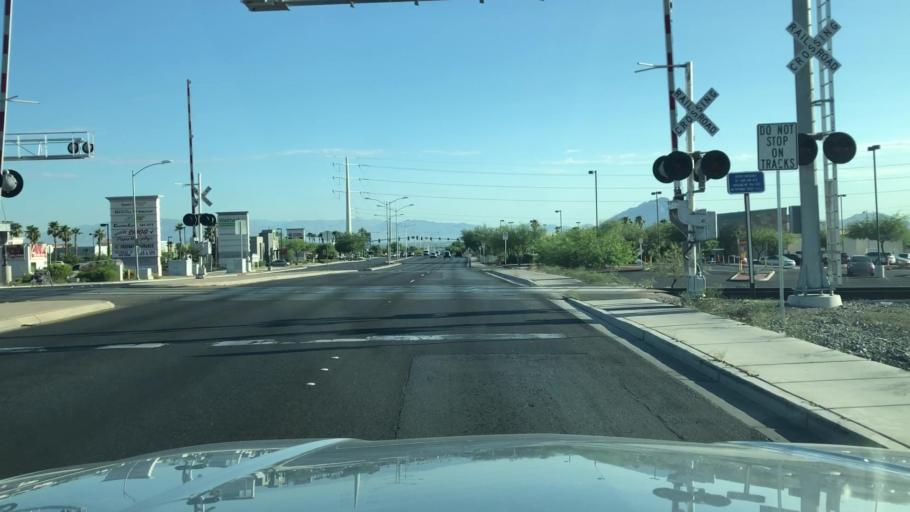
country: US
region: Nevada
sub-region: Clark County
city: Whitney
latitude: 36.0390
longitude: -115.0467
